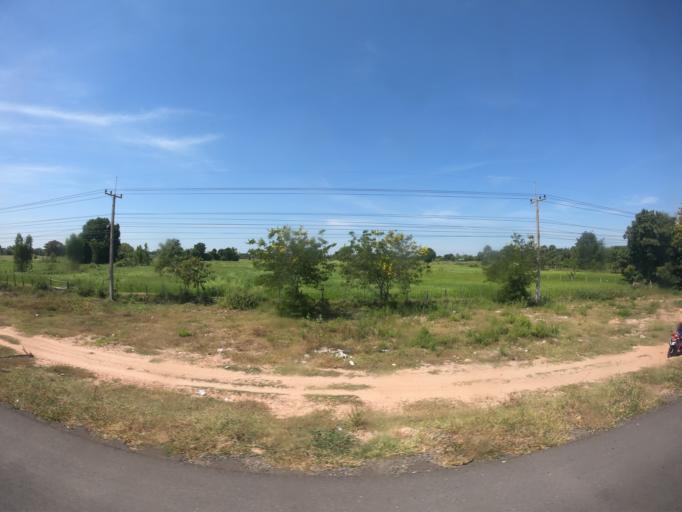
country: TH
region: Nakhon Ratchasima
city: Bua Lai
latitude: 15.6869
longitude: 102.5788
